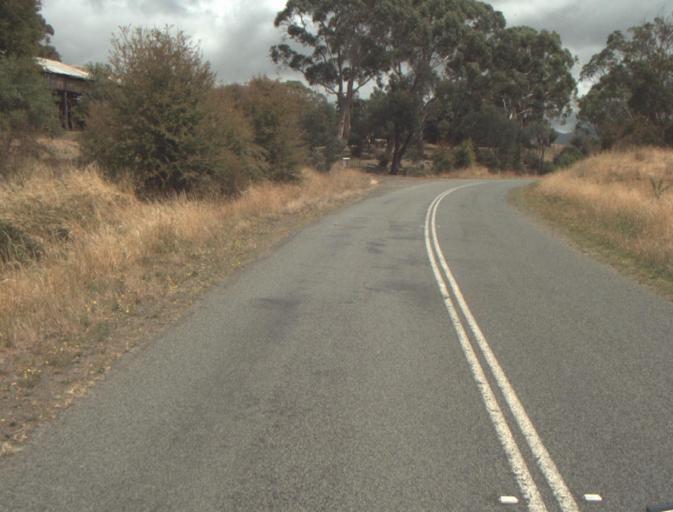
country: AU
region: Tasmania
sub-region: Northern Midlands
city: Evandale
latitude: -41.5025
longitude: 147.4752
